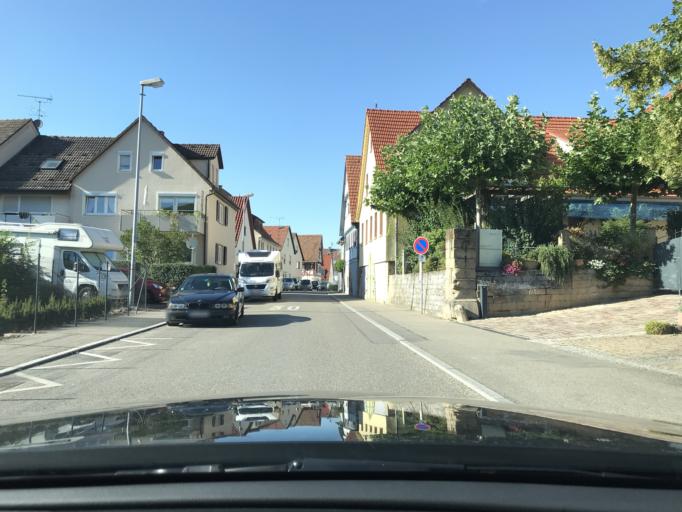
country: DE
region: Baden-Wuerttemberg
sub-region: Regierungsbezirk Stuttgart
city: Weinstadt-Endersbach
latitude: 48.7855
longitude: 9.3418
